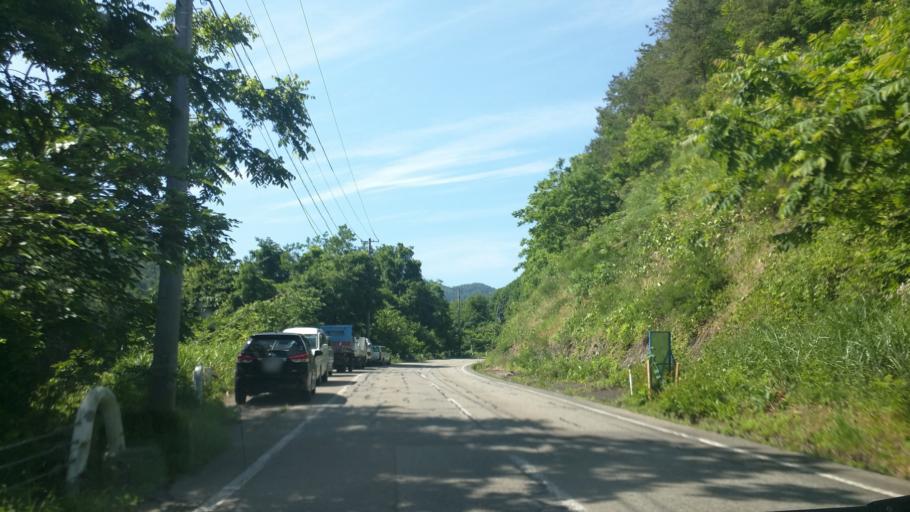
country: JP
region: Fukushima
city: Kitakata
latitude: 37.3984
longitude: 139.8717
